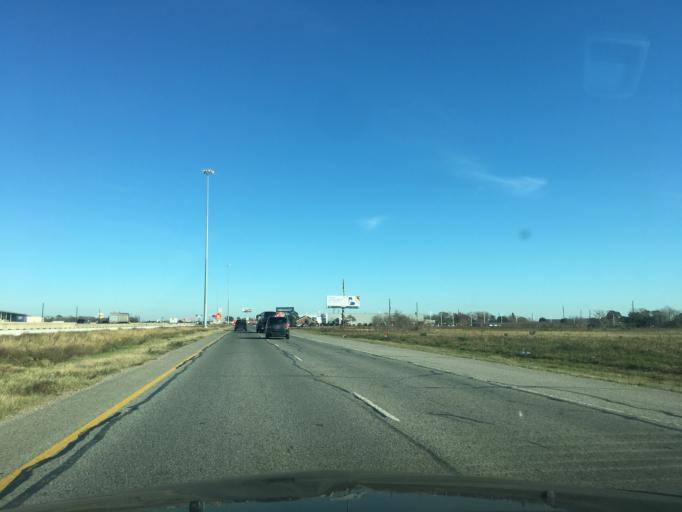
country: US
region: Texas
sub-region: Fort Bend County
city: Rosenberg
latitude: 29.5324
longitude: -95.7904
